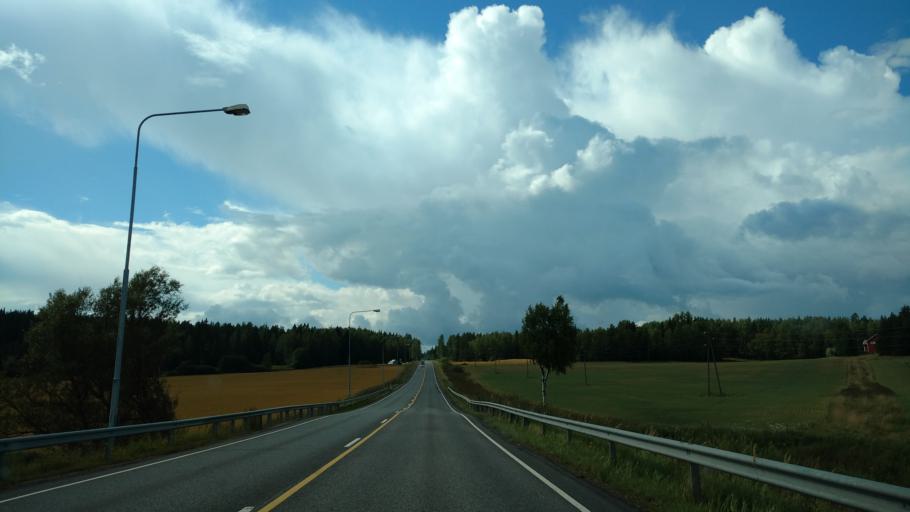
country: FI
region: Varsinais-Suomi
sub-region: Turku
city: Paimio
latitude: 60.4187
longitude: 22.7515
